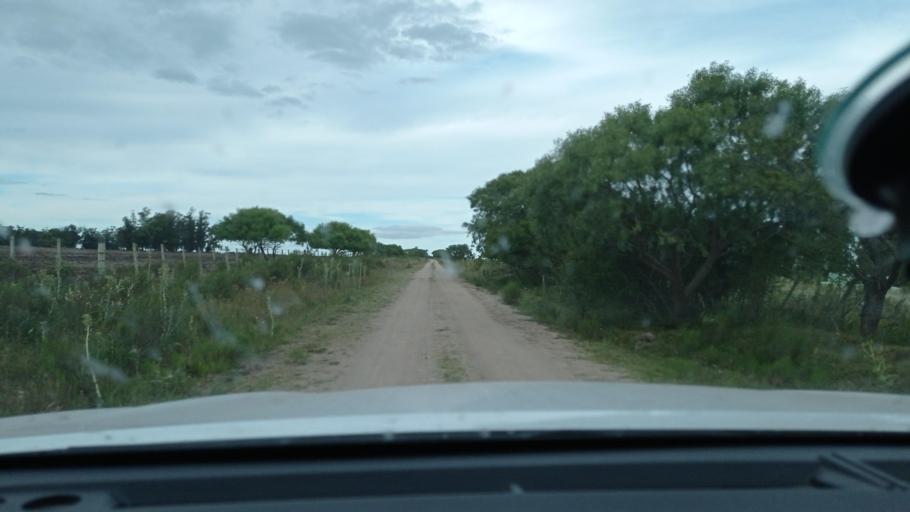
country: UY
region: Florida
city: Casupa
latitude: -34.1181
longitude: -55.8222
